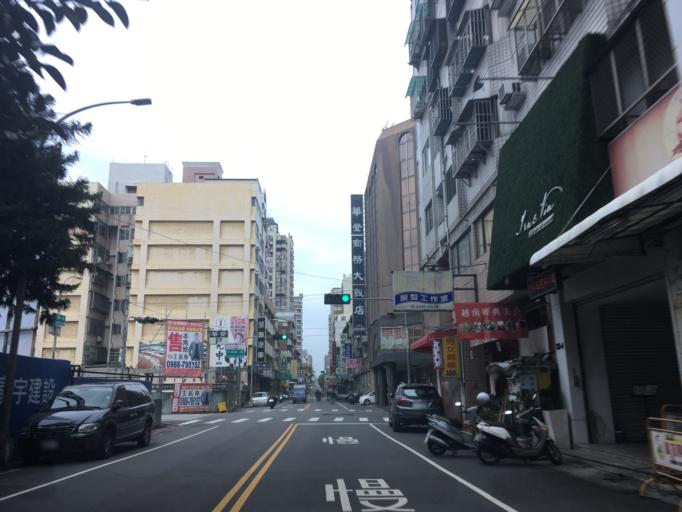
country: TW
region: Taiwan
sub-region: Taichung City
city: Taichung
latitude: 24.1743
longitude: 120.6770
